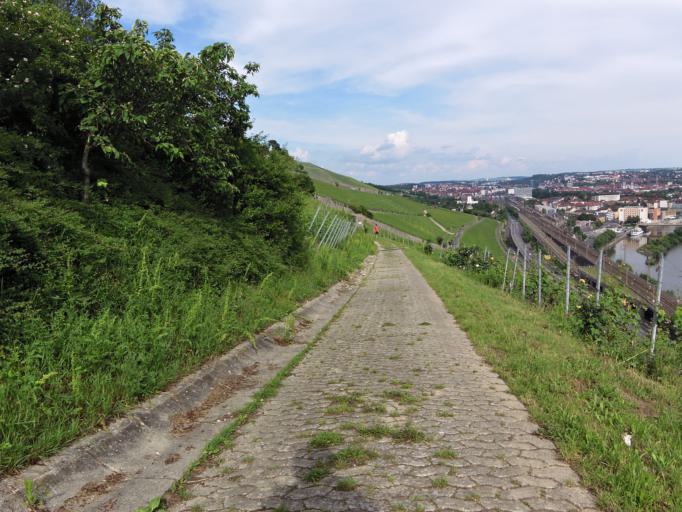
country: DE
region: Bavaria
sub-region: Regierungsbezirk Unterfranken
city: Hochberg
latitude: 49.8055
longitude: 9.9113
